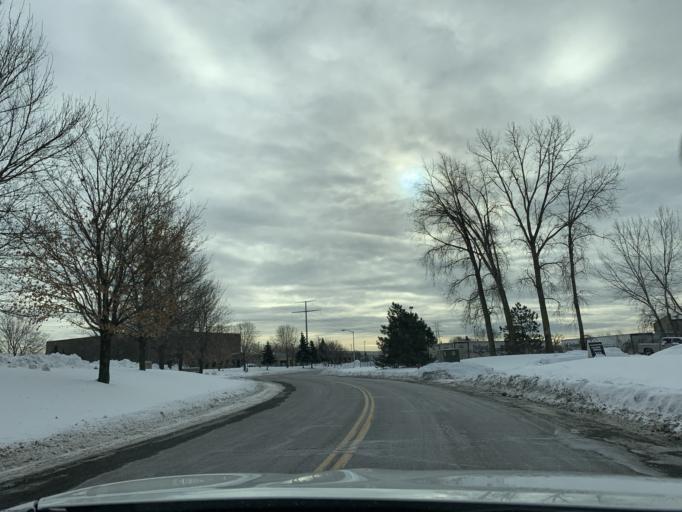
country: US
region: Minnesota
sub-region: Hennepin County
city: West Coon Rapids
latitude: 45.1775
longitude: -93.2979
